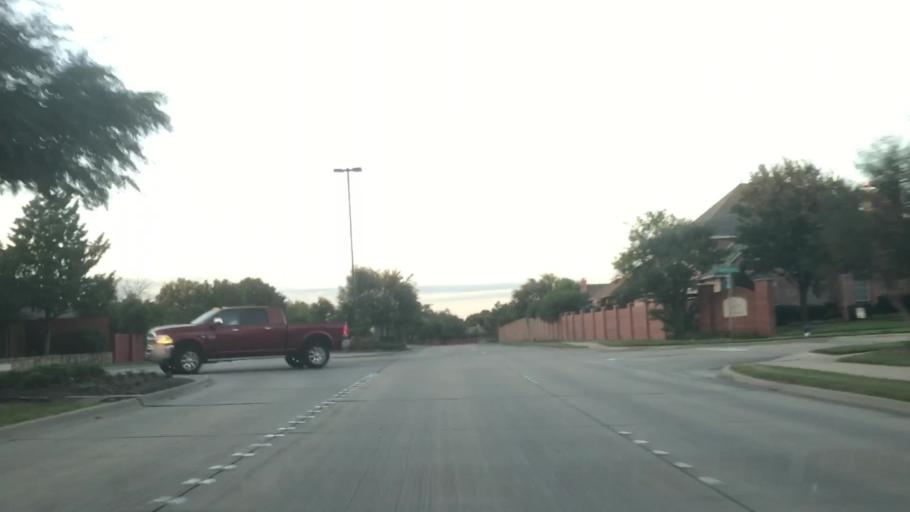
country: US
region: Texas
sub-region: Dallas County
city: Carrollton
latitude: 32.9779
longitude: -96.8727
